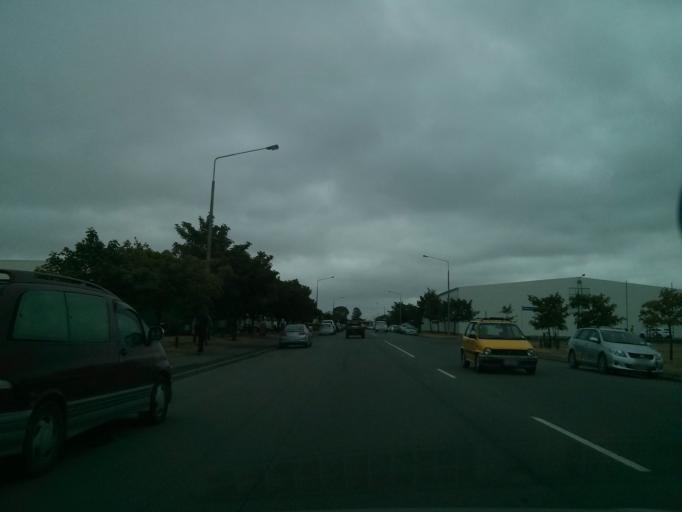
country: NZ
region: Canterbury
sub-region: Selwyn District
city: Prebbleton
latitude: -43.5379
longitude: 172.5375
